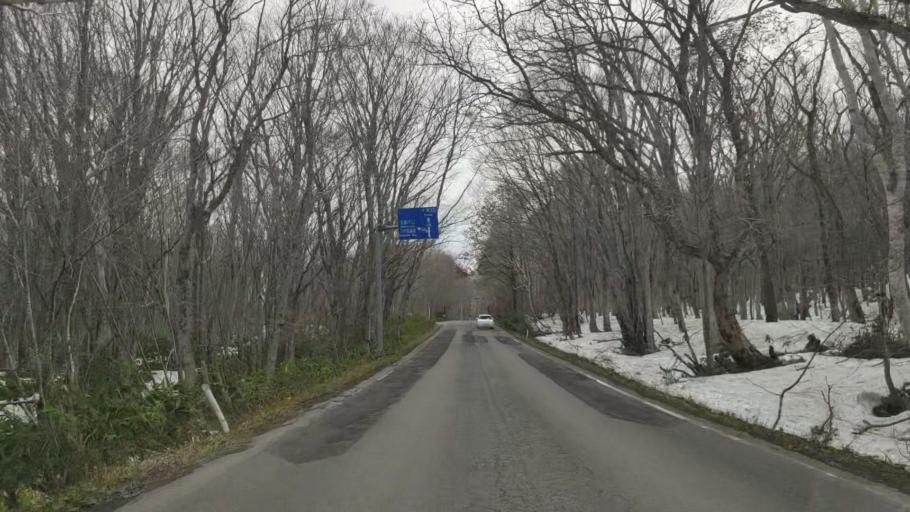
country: JP
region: Aomori
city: Aomori Shi
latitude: 40.6975
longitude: 140.9042
